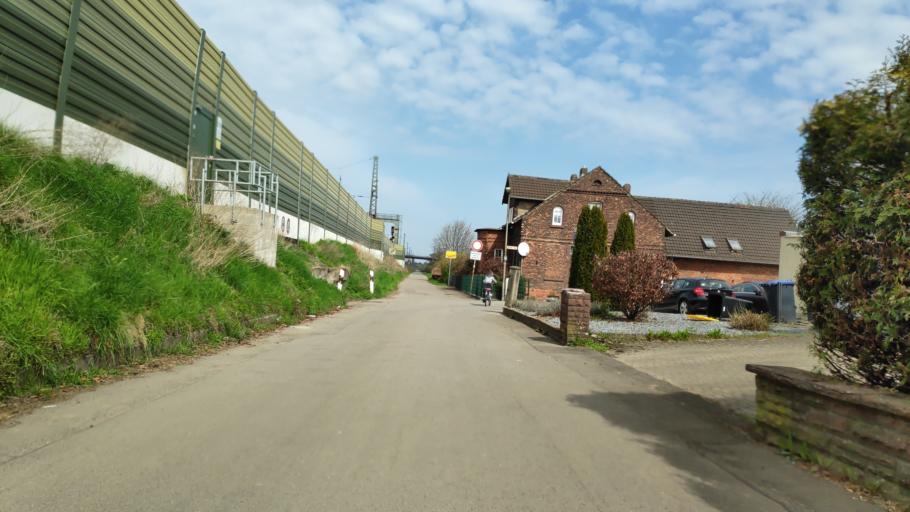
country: DE
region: North Rhine-Westphalia
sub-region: Regierungsbezirk Detmold
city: Minden
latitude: 52.2681
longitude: 8.9331
